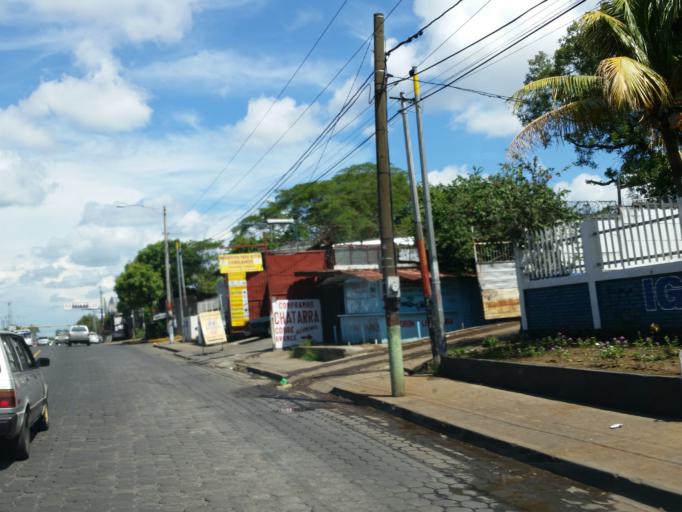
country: NI
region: Managua
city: Managua
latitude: 12.1299
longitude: -86.2289
